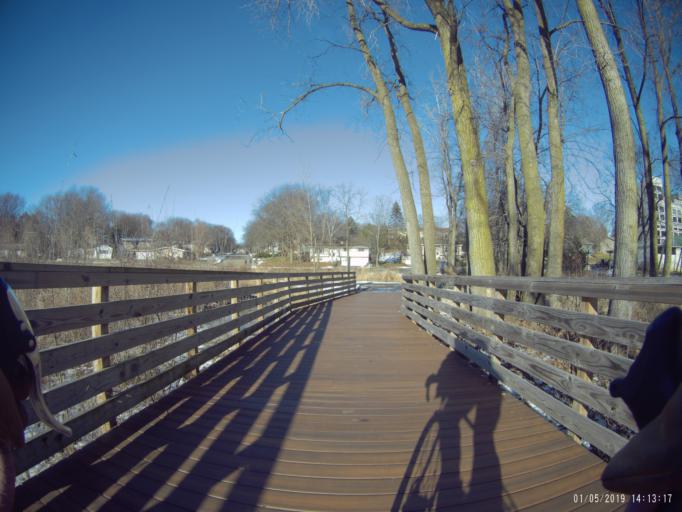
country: US
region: Wisconsin
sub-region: Dane County
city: Shorewood Hills
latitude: 43.0257
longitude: -89.4521
